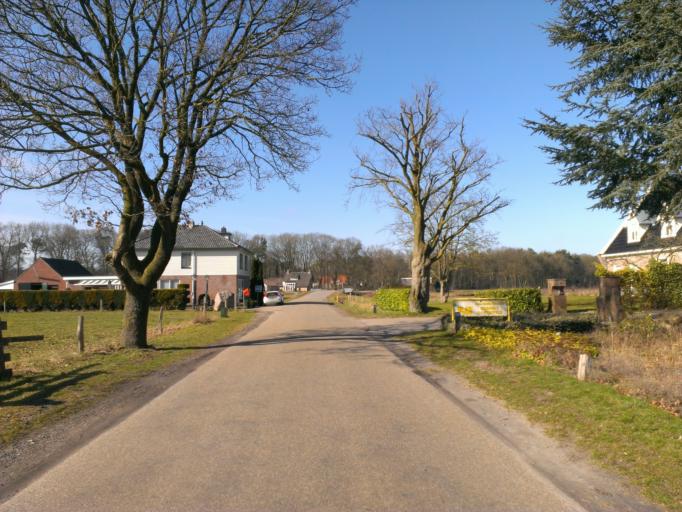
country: NL
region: Overijssel
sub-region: Gemeente Almelo
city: Almelo
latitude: 52.3240
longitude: 6.6883
